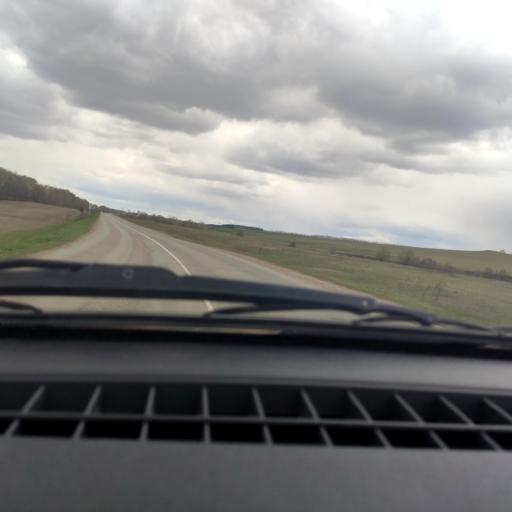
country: RU
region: Bashkortostan
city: Chekmagush
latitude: 55.1193
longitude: 54.7481
